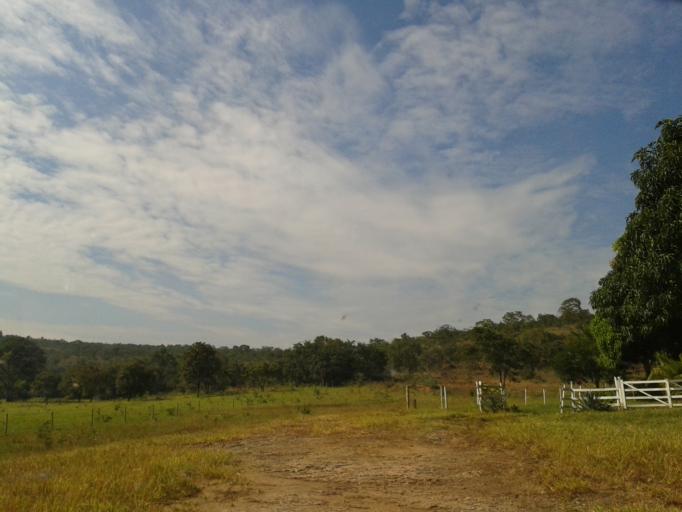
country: BR
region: Minas Gerais
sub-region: Campina Verde
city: Campina Verde
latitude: -19.3968
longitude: -49.6259
